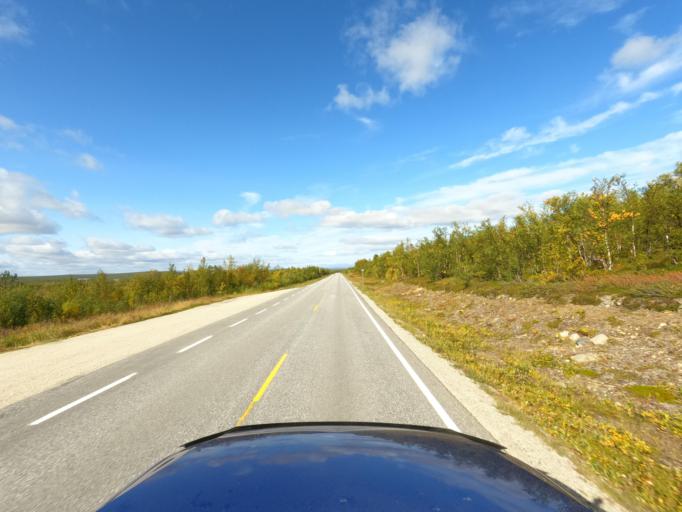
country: NO
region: Finnmark Fylke
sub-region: Karasjok
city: Karasjohka
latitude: 69.5612
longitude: 25.3893
